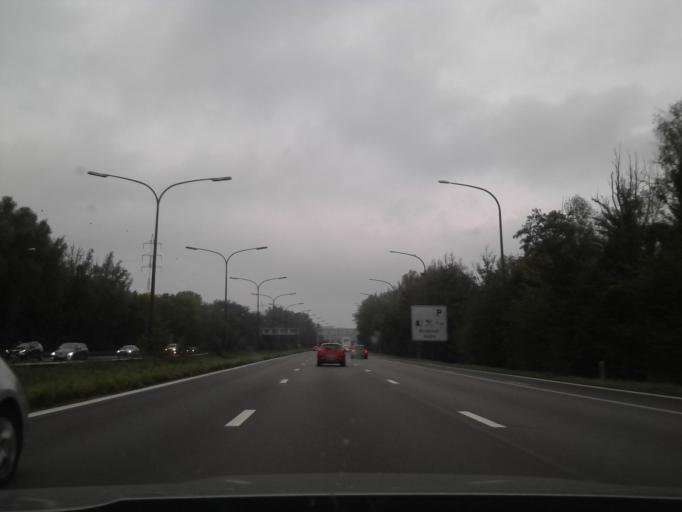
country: BE
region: Flanders
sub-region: Provincie Vlaams-Brabant
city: Drogenbos
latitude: 50.7883
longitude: 4.3039
